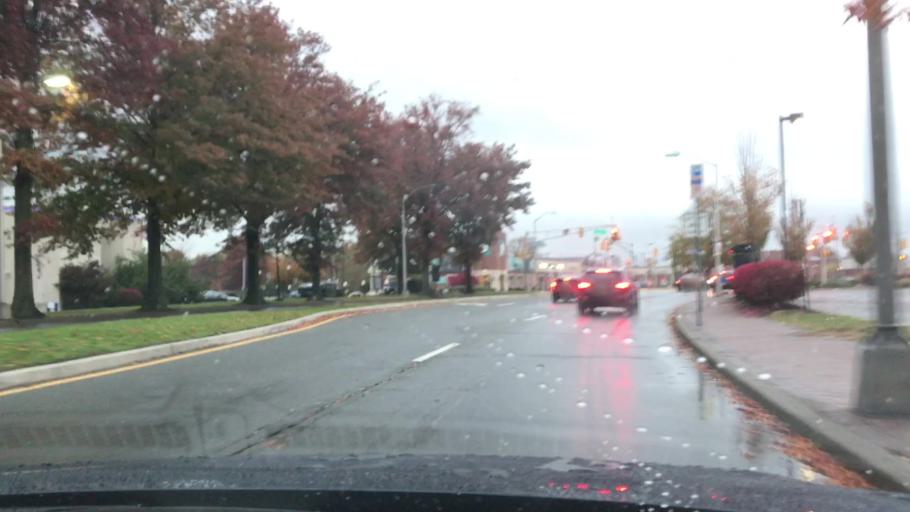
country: US
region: New Jersey
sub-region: Bergen County
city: Lodi
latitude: 40.8756
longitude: -74.0875
